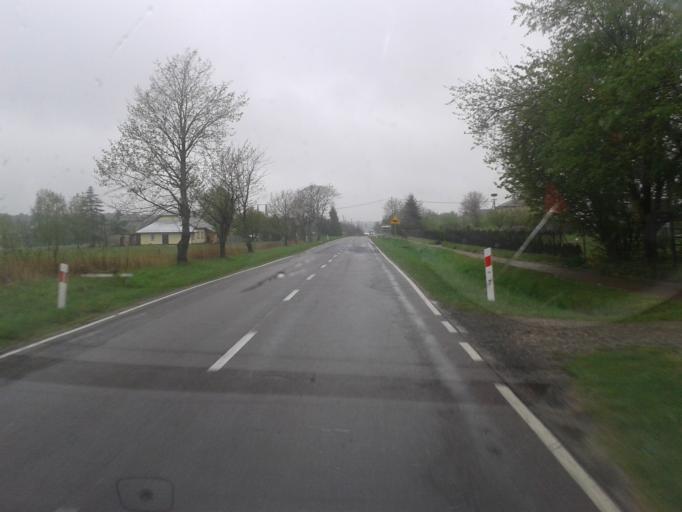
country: PL
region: Subcarpathian Voivodeship
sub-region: Powiat lubaczowski
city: Nowe Siolo
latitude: 50.2817
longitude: 23.1697
